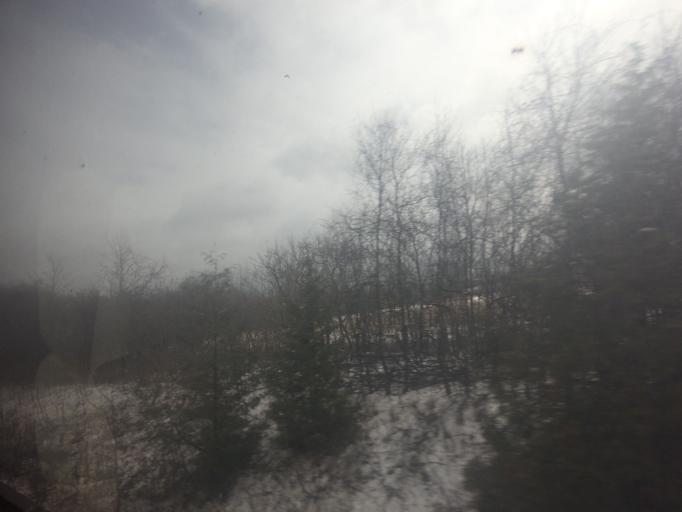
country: CA
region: Ontario
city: Cobourg
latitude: 43.9398
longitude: -78.3928
